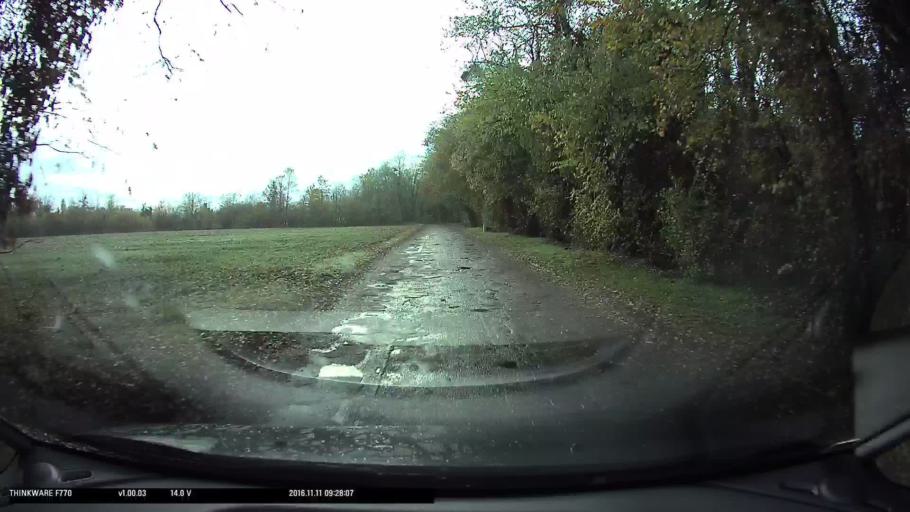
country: FR
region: Ile-de-France
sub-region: Departement du Val-d'Oise
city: Osny
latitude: 49.0719
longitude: 2.0408
